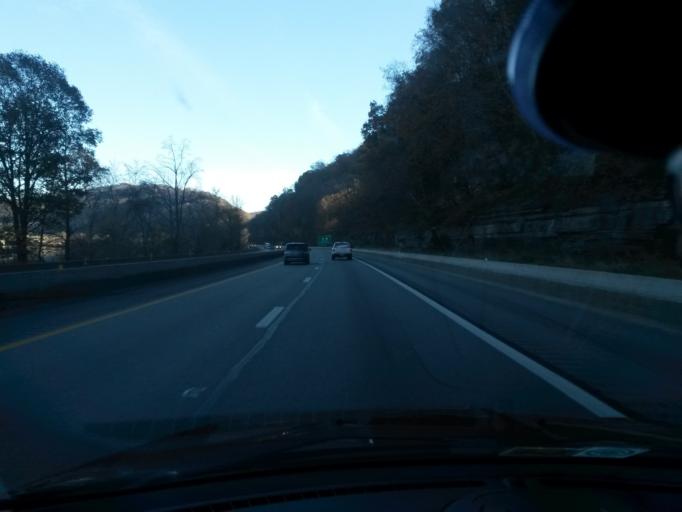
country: US
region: West Virginia
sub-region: Kanawha County
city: Chesapeake
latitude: 38.2023
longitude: -81.5150
